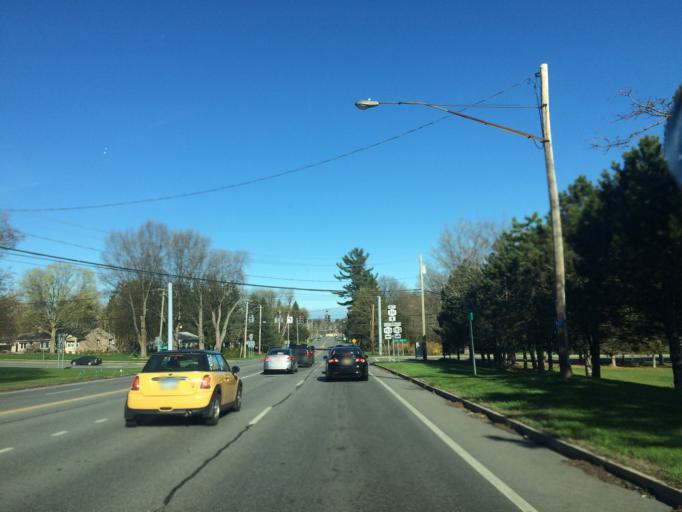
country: US
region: New York
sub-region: Monroe County
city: East Rochester
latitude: 43.1080
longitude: -77.4987
